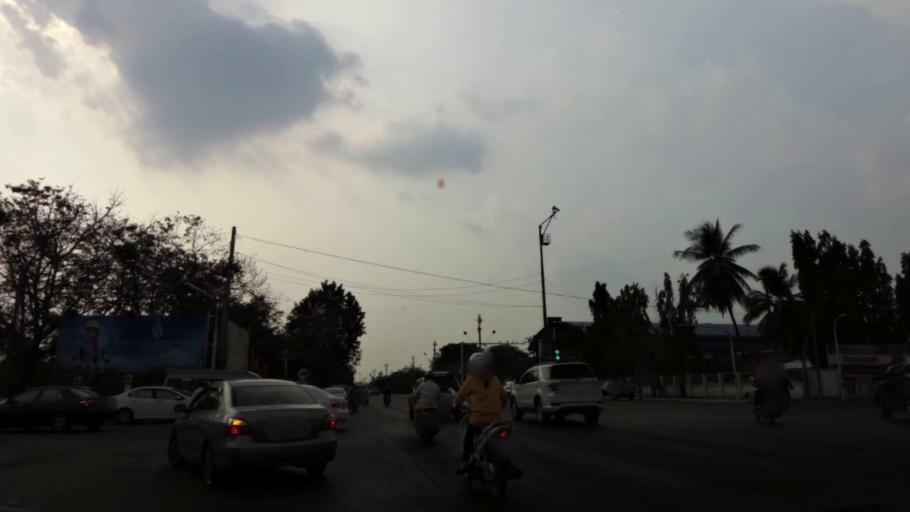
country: TH
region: Phra Nakhon Si Ayutthaya
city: Phra Nakhon Si Ayutthaya
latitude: 14.3646
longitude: 100.5603
